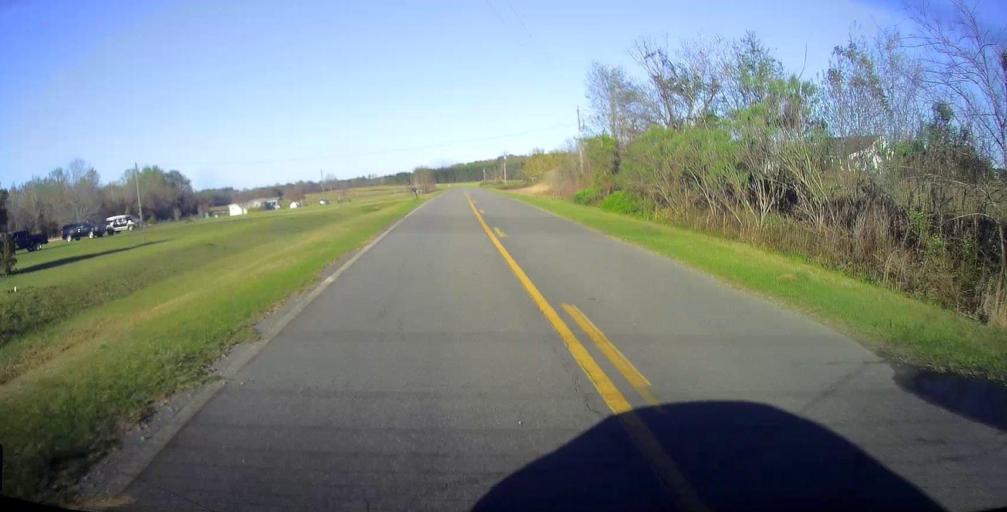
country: US
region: Georgia
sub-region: Pulaski County
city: Hawkinsville
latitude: 32.3135
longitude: -83.5761
